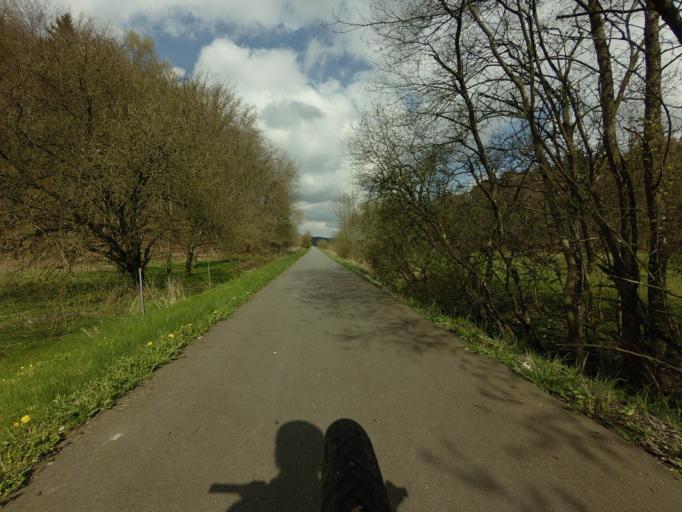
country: DK
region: North Denmark
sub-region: Mariagerfjord Kommune
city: Hadsund
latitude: 56.8417
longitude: 10.1110
